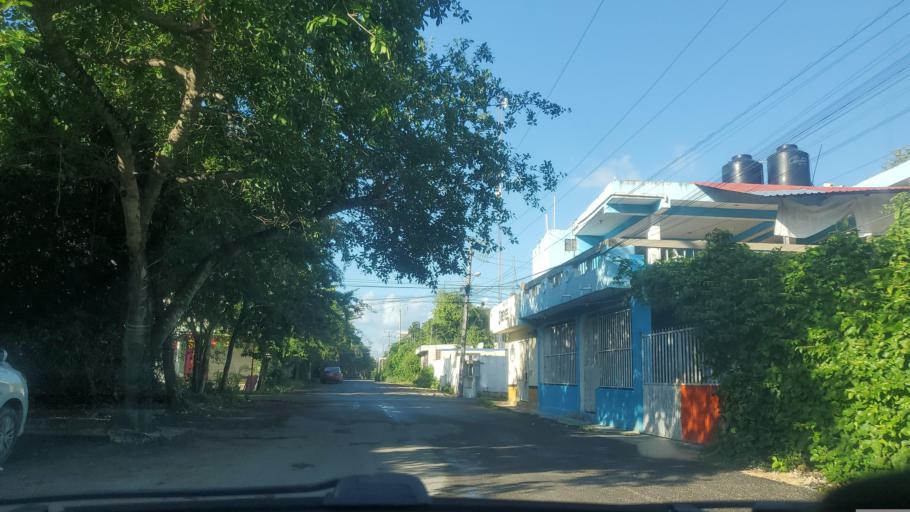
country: MX
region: Quintana Roo
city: Tulum
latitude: 20.2089
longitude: -87.4737
